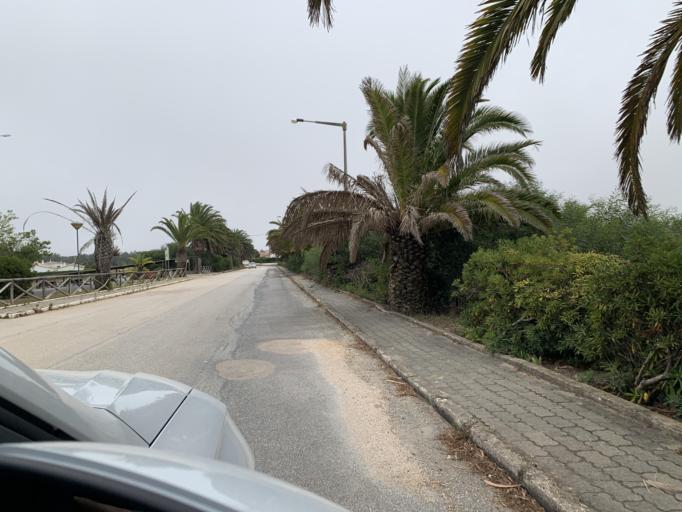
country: PT
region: Faro
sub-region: Aljezur
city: Aljezur
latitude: 37.3034
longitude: -8.8500
